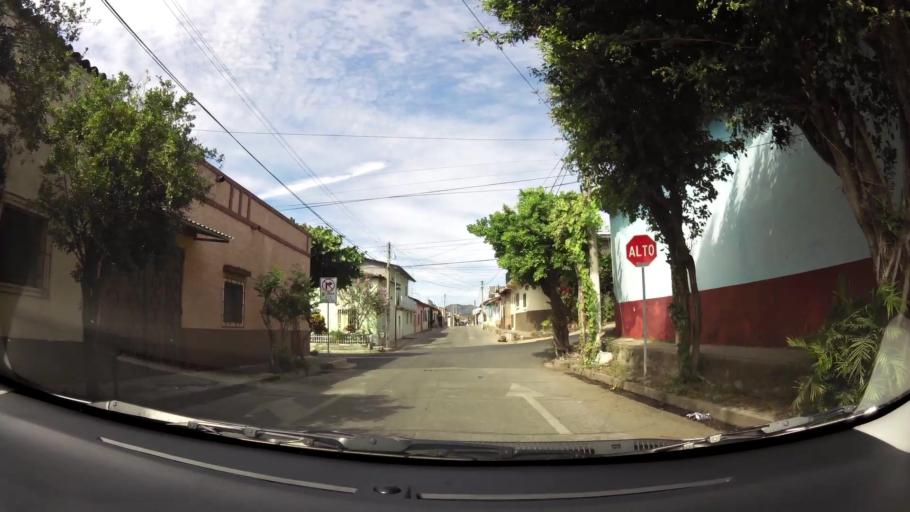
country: SV
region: Santa Ana
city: Chalchuapa
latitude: 13.9818
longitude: -89.6782
